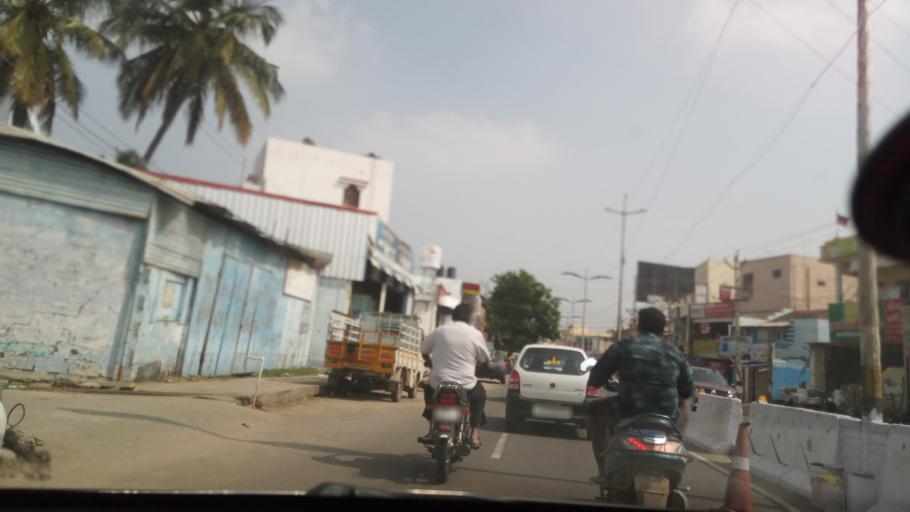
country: IN
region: Tamil Nadu
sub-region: Coimbatore
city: Perur
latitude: 11.0185
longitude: 76.9205
